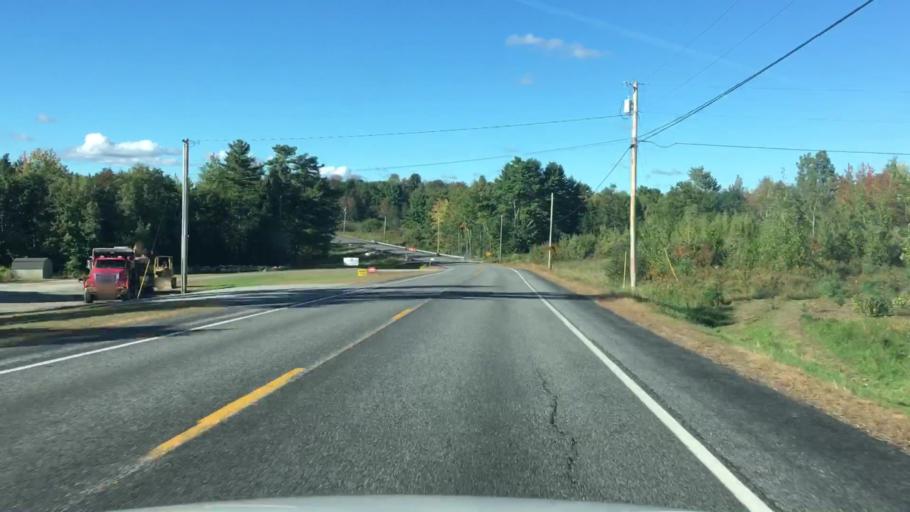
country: US
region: Maine
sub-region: Androscoggin County
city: Lisbon
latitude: 44.0462
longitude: -70.0773
